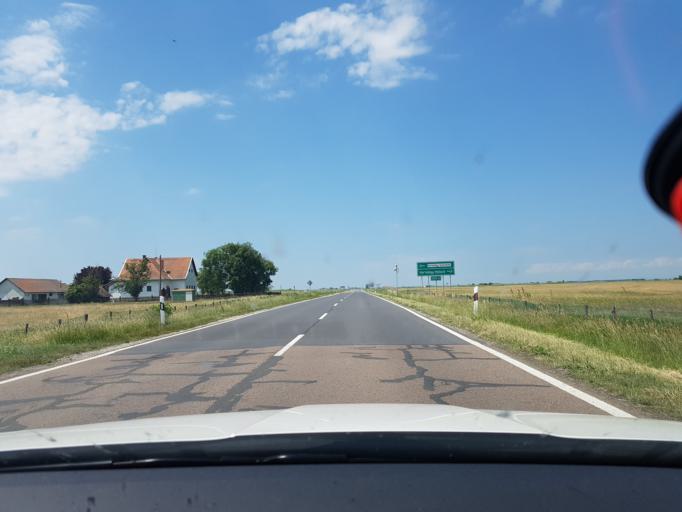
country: HU
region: Hajdu-Bihar
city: Hortobagy
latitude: 47.5905
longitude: 21.0830
